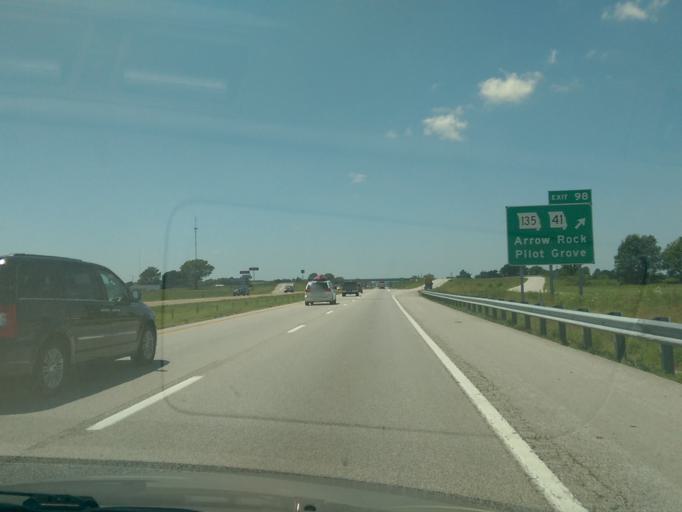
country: US
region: Missouri
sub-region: Cooper County
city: Boonville
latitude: 38.9353
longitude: -92.8414
